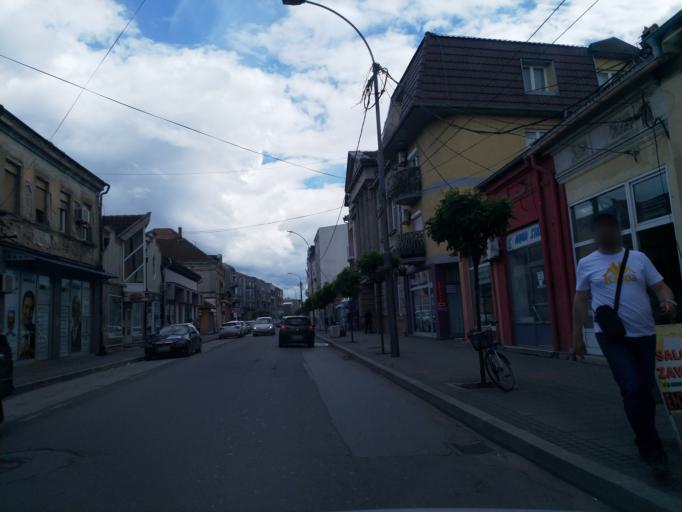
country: RS
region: Central Serbia
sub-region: Pomoravski Okrug
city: Cuprija
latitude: 43.9361
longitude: 21.3701
